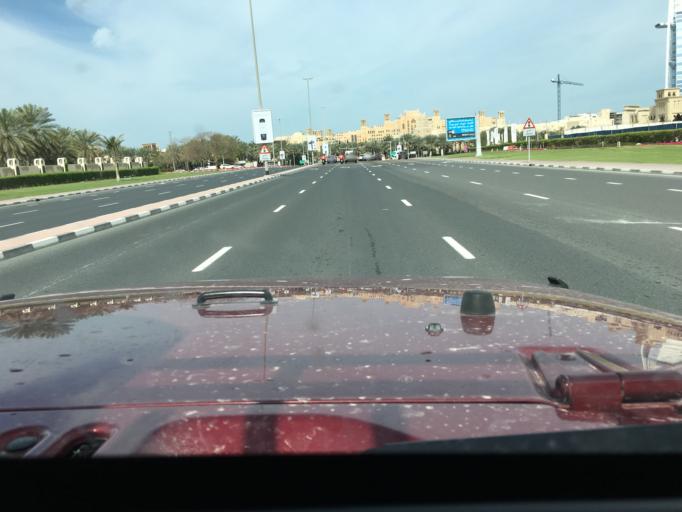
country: AE
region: Dubai
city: Dubai
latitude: 25.1316
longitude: 55.1900
